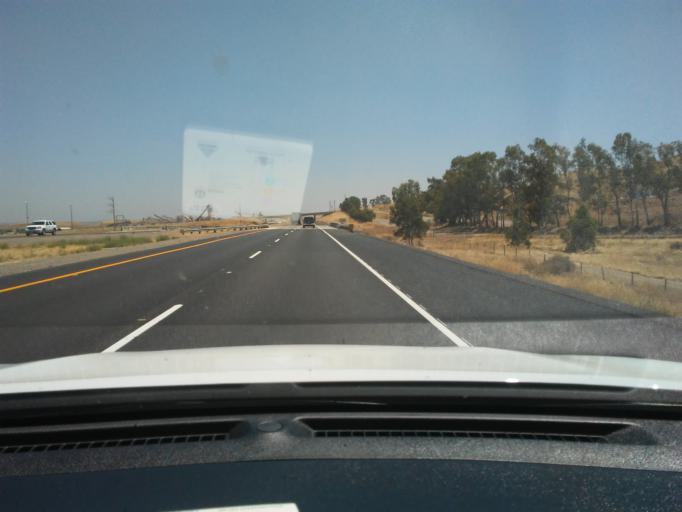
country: US
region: California
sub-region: San Joaquin County
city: Tracy
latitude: 37.6160
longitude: -121.3665
